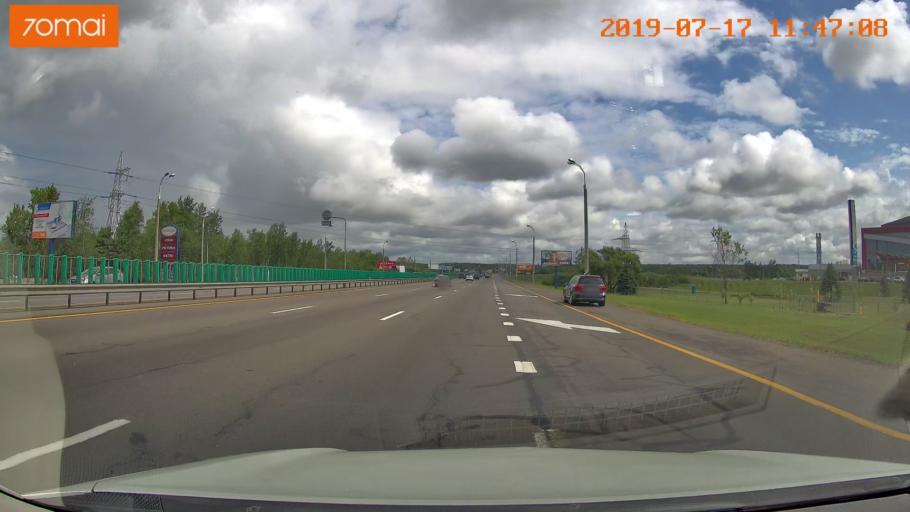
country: BY
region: Minsk
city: Zhdanovichy
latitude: 53.9533
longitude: 27.4491
